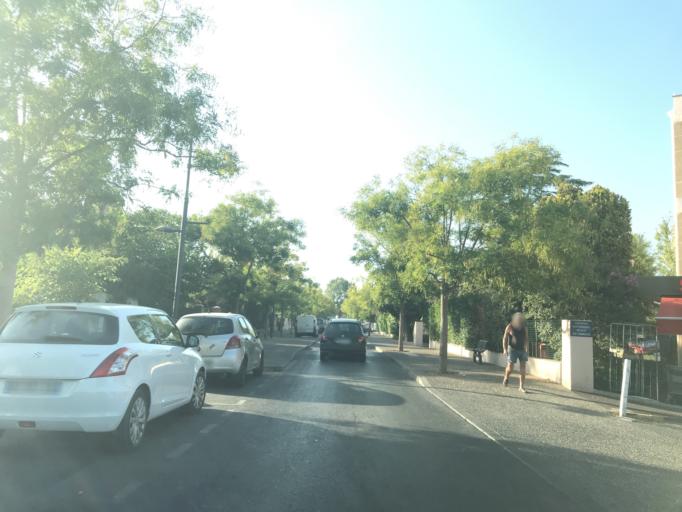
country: FR
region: Provence-Alpes-Cote d'Azur
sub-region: Departement du Var
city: Sanary-sur-Mer
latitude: 43.1147
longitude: 5.8110
